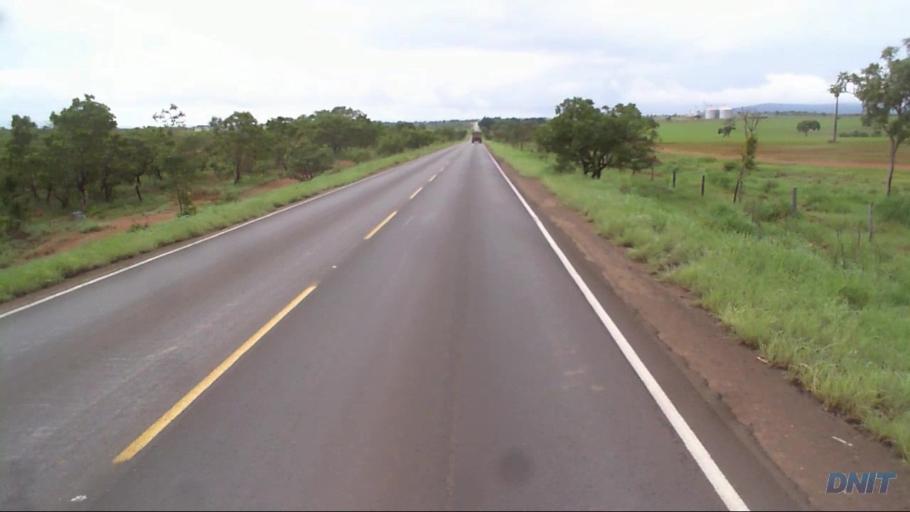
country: BR
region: Goias
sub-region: Padre Bernardo
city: Padre Bernardo
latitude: -15.2298
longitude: -48.2766
